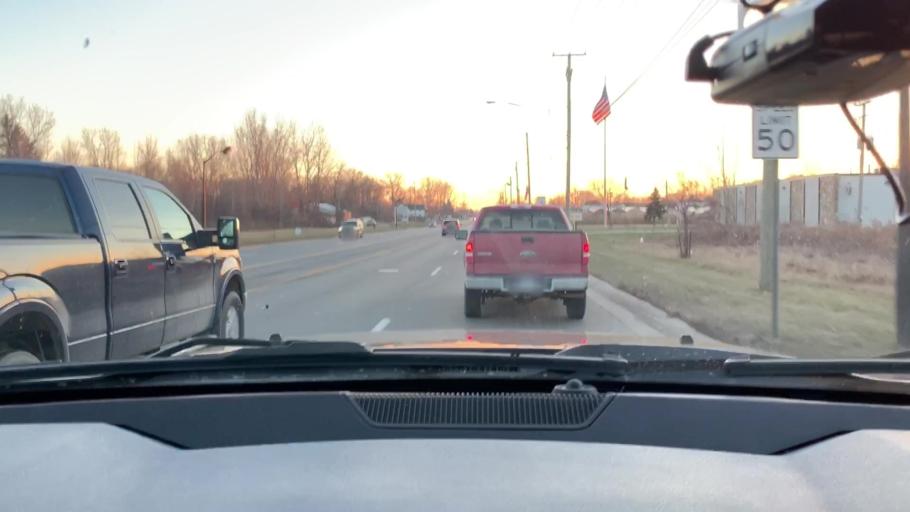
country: US
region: Michigan
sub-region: Wayne County
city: Woodhaven
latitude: 42.1301
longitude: -83.2717
